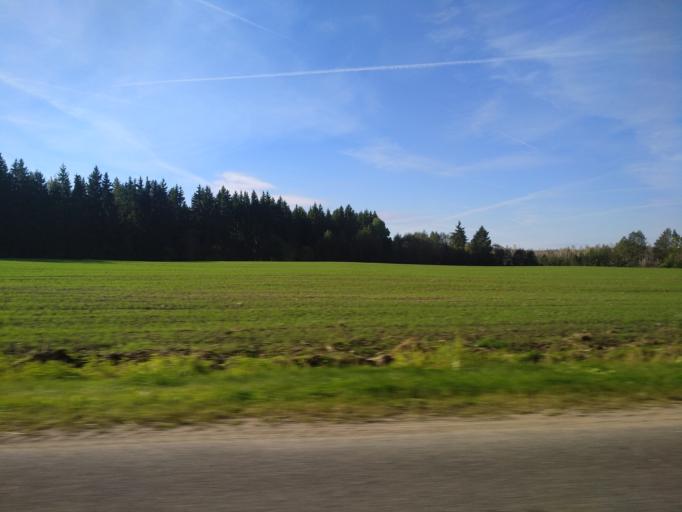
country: BY
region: Vitebsk
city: Mosar
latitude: 55.1446
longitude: 27.1799
